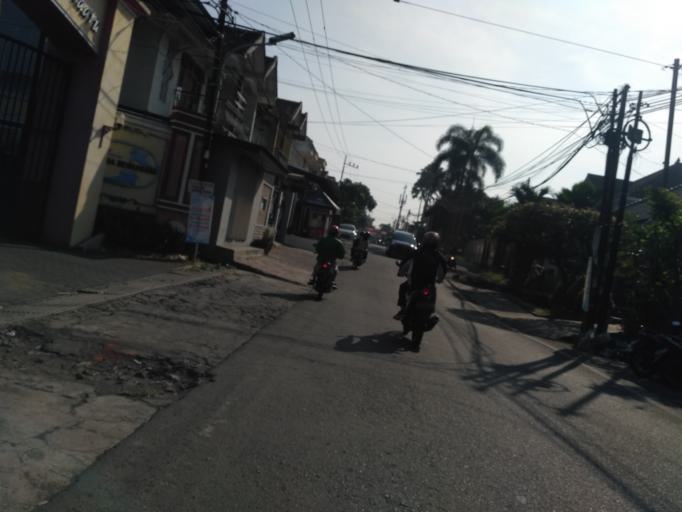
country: ID
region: East Java
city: Malang
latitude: -7.9490
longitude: 112.6238
